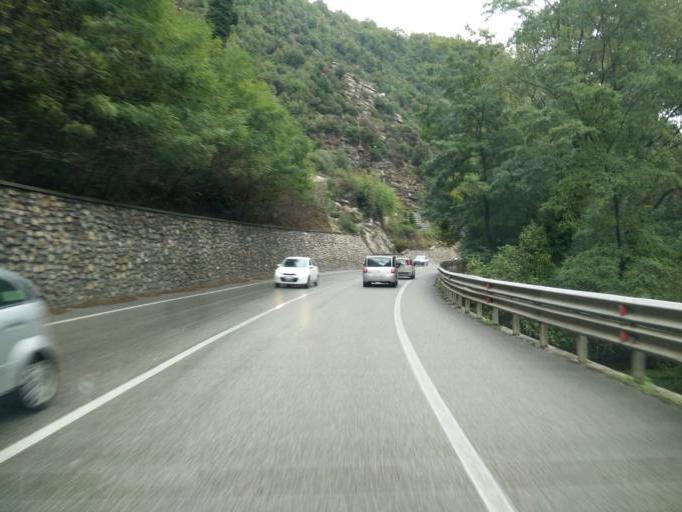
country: IT
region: Tuscany
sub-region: Provincia di Lucca
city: Valdottavo
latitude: 43.9298
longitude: 10.5123
